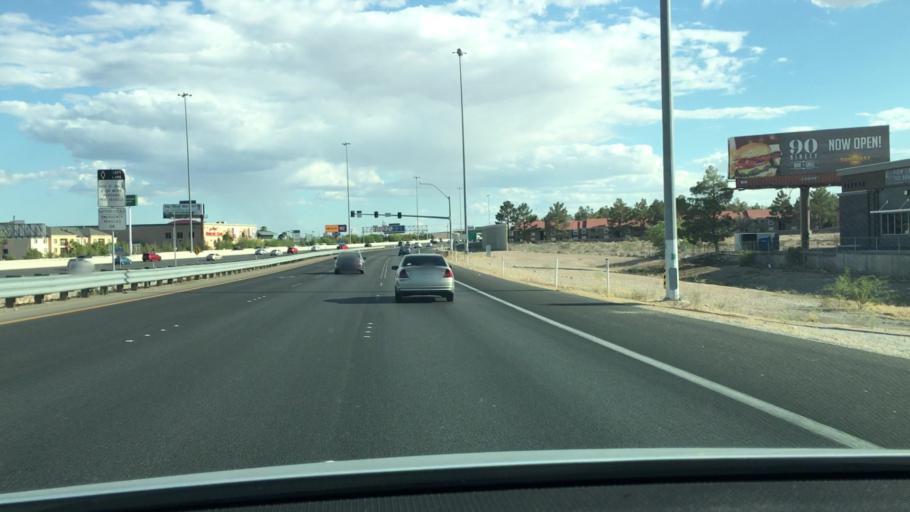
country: US
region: Nevada
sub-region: Clark County
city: Spring Valley
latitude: 36.1951
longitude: -115.2455
